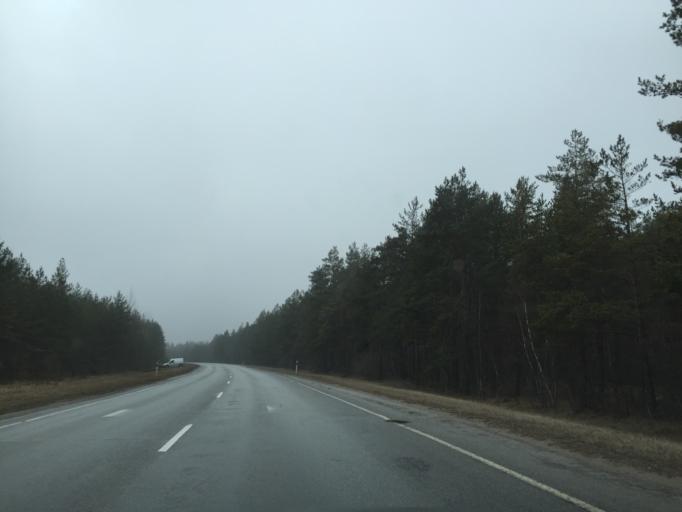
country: EE
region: Laeaene
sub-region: Lihula vald
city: Lihula
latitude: 58.6071
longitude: 23.5613
